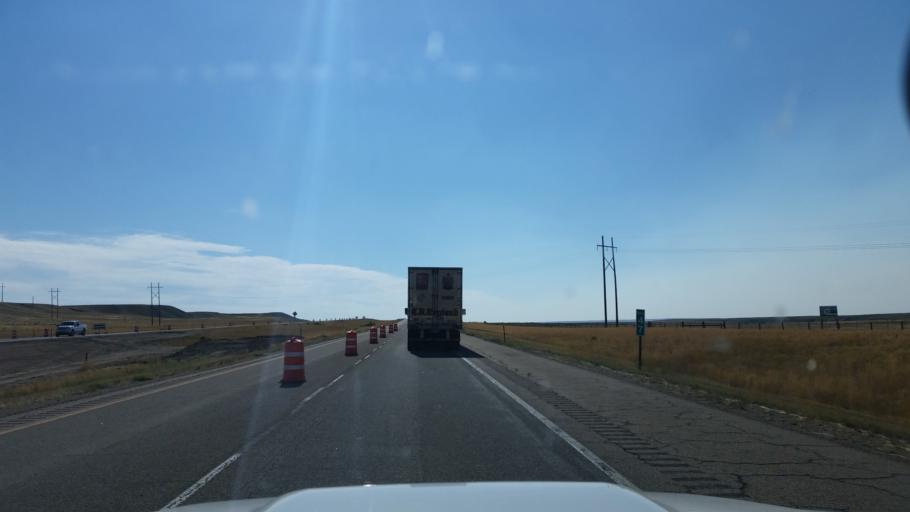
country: US
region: Wyoming
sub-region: Uinta County
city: Lyman
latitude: 41.3877
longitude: -110.2086
